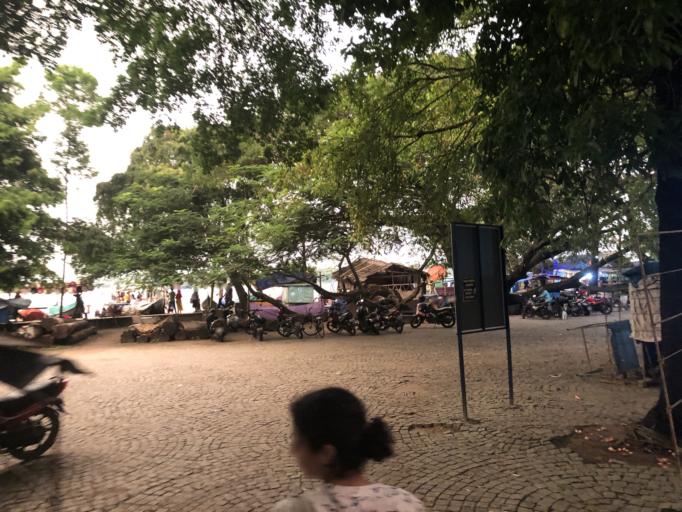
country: IN
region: Kerala
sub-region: Ernakulam
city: Cochin
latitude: 9.9675
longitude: 76.2415
